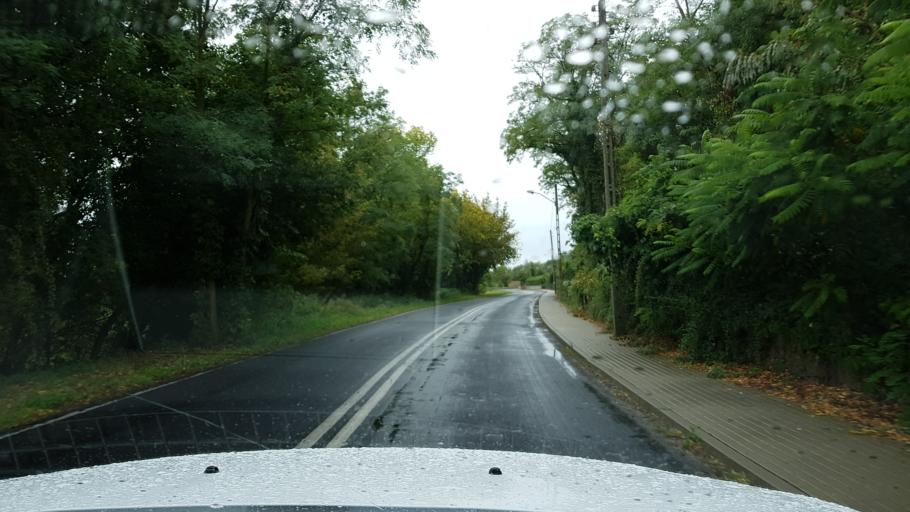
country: PL
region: West Pomeranian Voivodeship
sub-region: Powiat gryfinski
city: Cedynia
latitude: 52.8323
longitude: 14.1828
